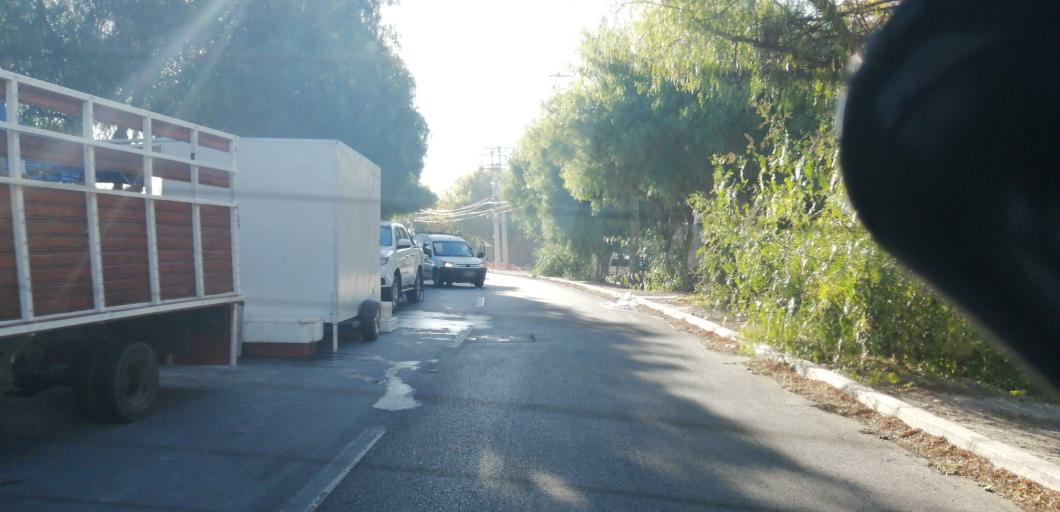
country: CL
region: Santiago Metropolitan
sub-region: Provincia de Santiago
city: Lo Prado
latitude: -33.4528
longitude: -70.8517
